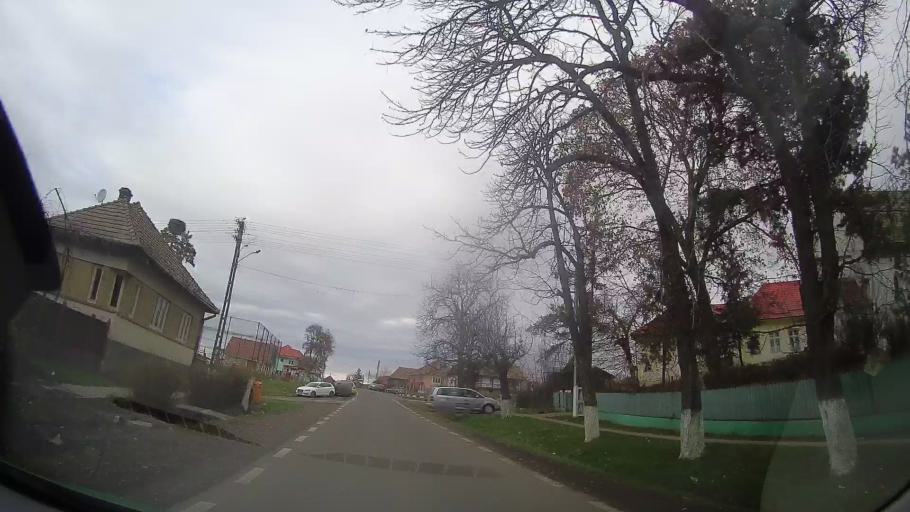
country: RO
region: Mures
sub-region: Comuna Faragau
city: Faragau
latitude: 46.7803
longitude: 24.5524
